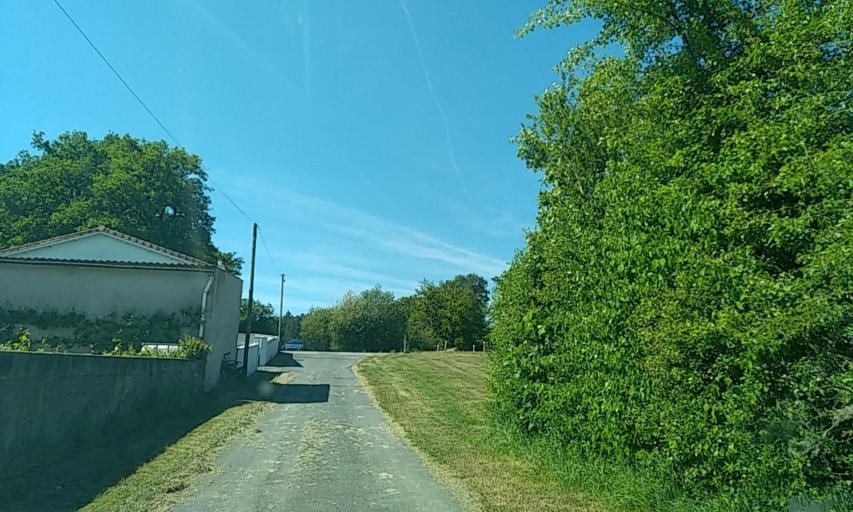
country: FR
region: Poitou-Charentes
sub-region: Departement des Deux-Sevres
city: Boisme
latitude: 46.7733
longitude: -0.4384
